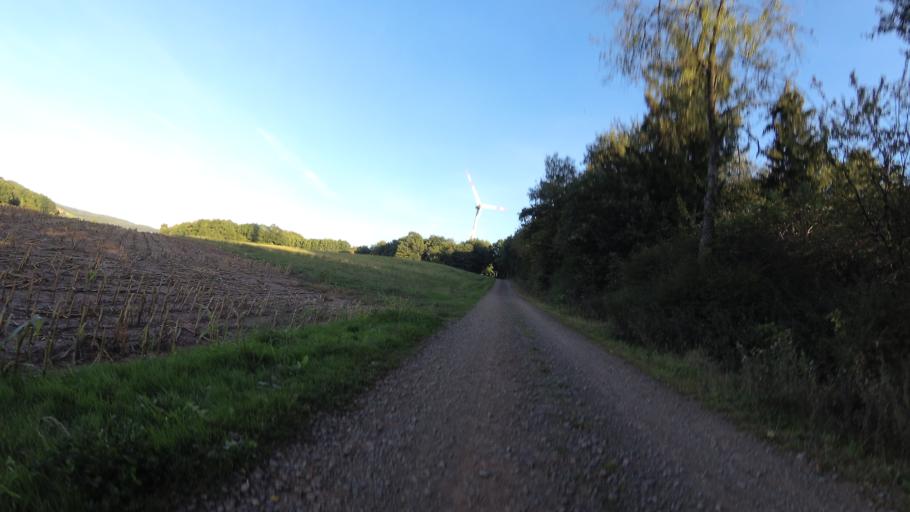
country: DE
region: Saarland
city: Sankt Wendel
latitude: 49.4423
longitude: 7.2061
